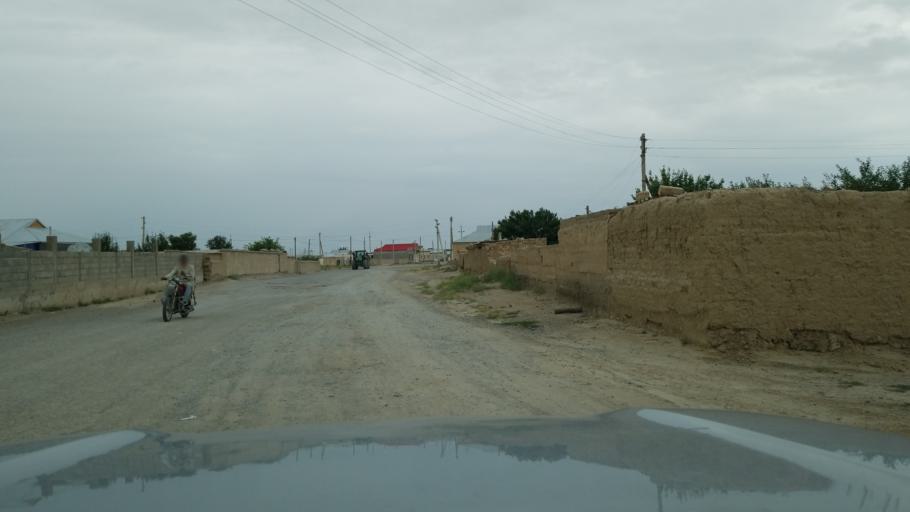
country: TM
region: Balkan
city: Serdar
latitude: 38.9898
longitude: 56.2773
